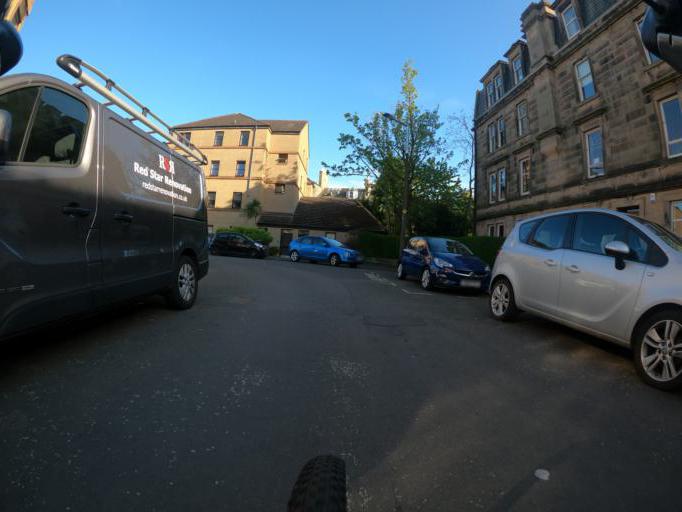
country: GB
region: Scotland
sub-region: Edinburgh
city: Edinburgh
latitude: 55.9750
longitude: -3.1872
